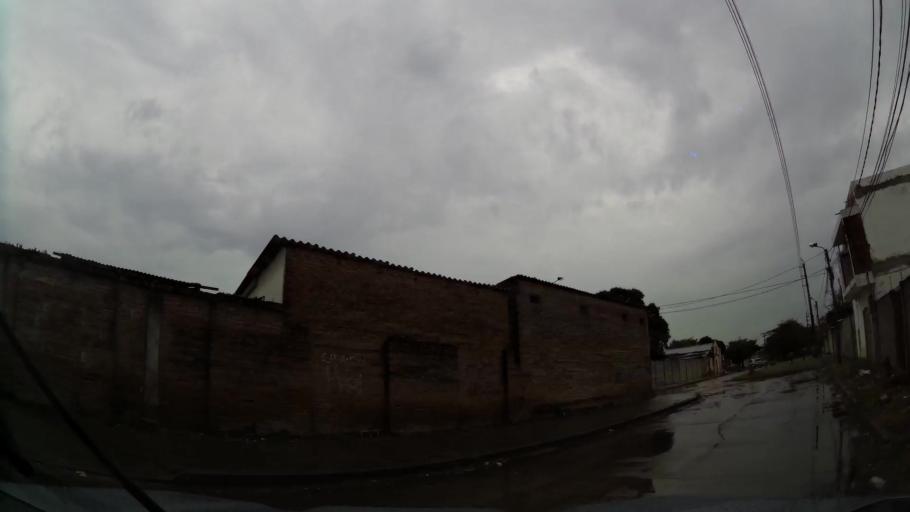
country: BO
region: Santa Cruz
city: Santa Cruz de la Sierra
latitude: -17.7842
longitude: -63.1543
